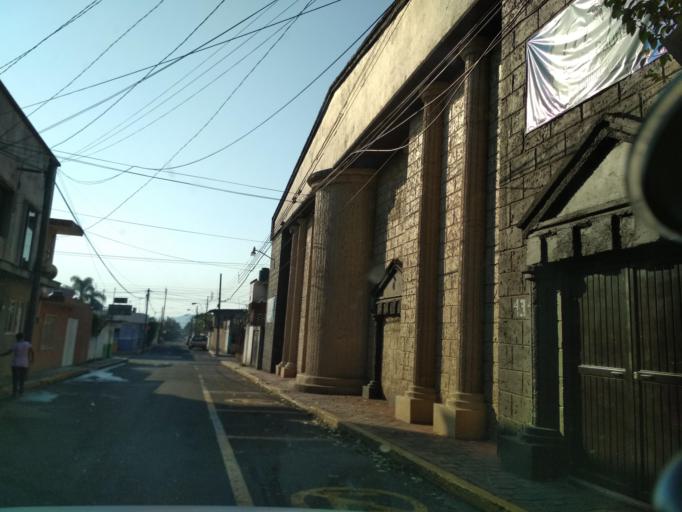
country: MX
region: Veracruz
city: Ixtac Zoquitlan
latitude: 18.8611
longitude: -97.0783
